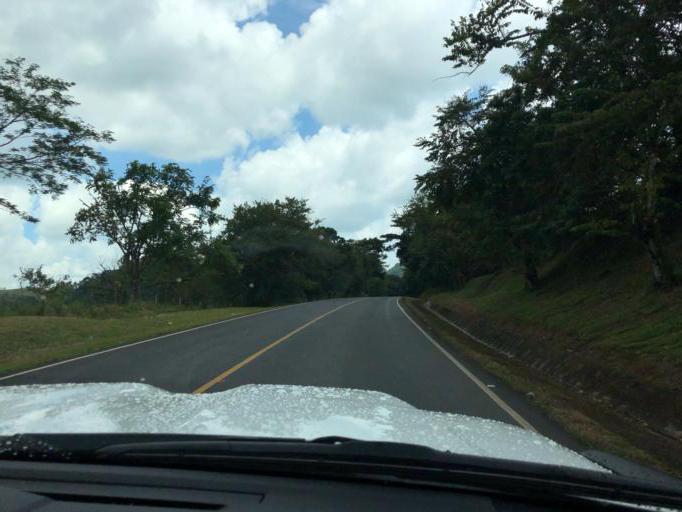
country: NI
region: Chontales
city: Villa Sandino
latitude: 11.9968
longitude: -84.9211
